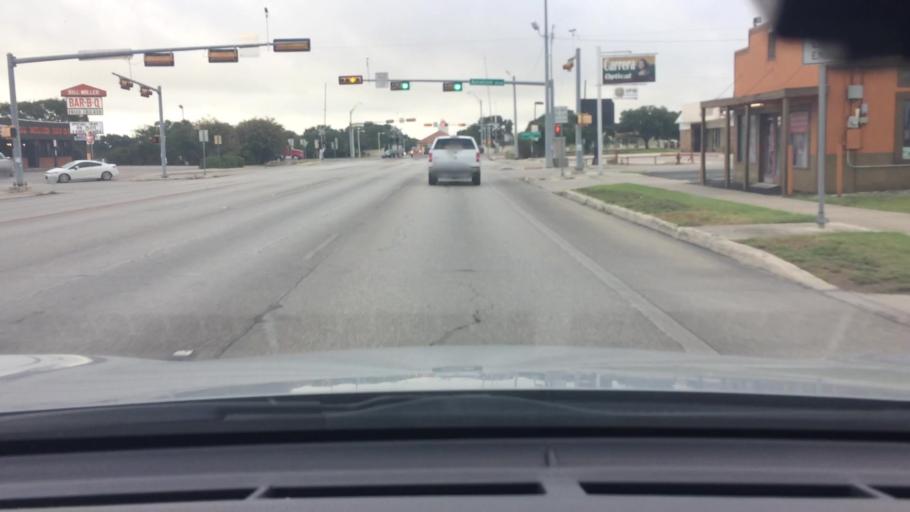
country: US
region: Texas
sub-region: Bexar County
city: Universal City
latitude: 29.5452
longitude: -98.2889
